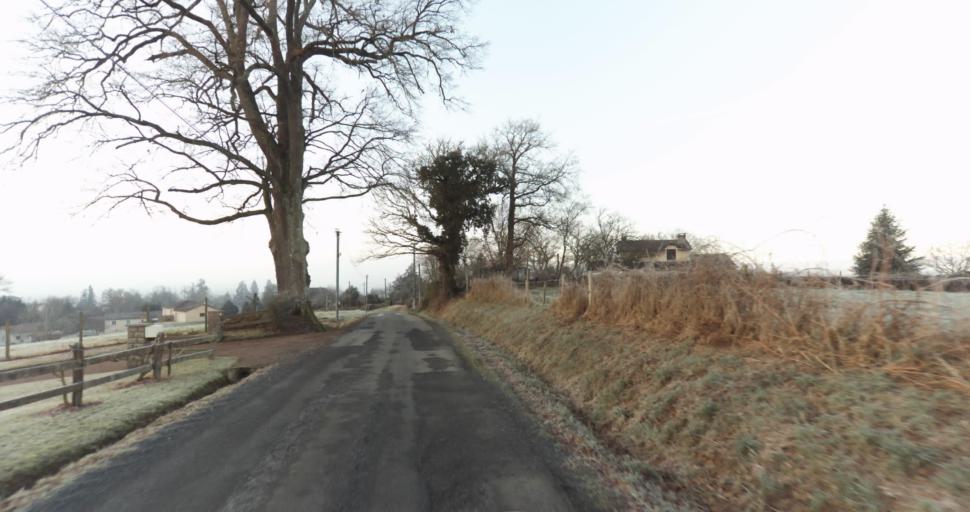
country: FR
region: Limousin
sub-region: Departement de la Haute-Vienne
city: Aixe-sur-Vienne
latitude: 45.8049
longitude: 1.1280
